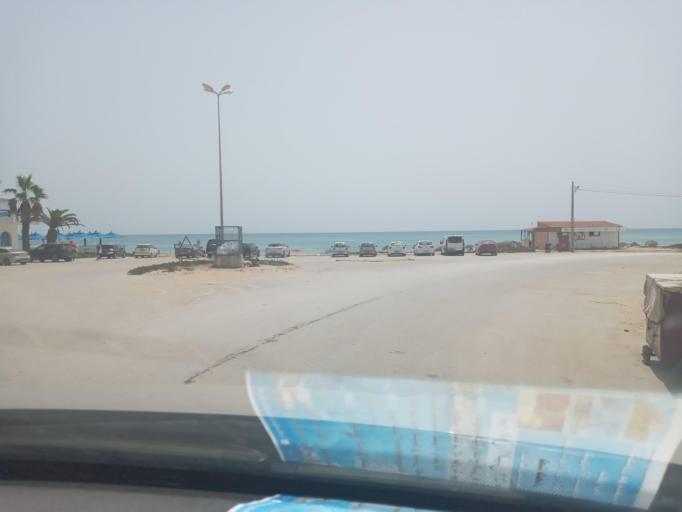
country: TN
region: Nabul
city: El Haouaria
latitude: 37.0358
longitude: 11.0583
